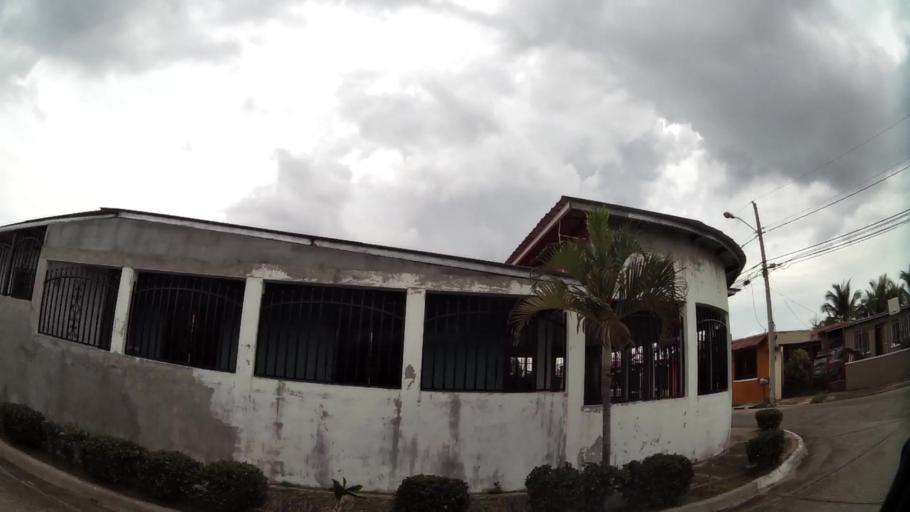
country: PA
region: Panama
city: Tocumen
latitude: 9.0521
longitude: -79.4111
